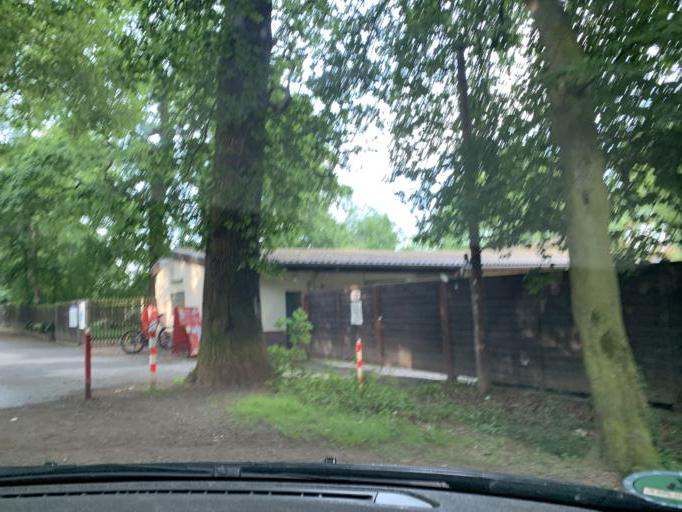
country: DE
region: North Rhine-Westphalia
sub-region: Regierungsbezirk Koln
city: Kreuzau
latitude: 50.7645
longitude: 6.5029
